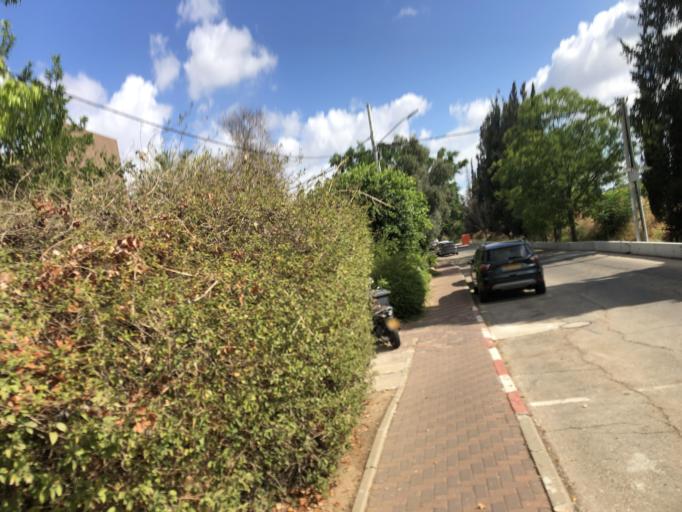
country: IL
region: Central District
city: Yehud
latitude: 32.0340
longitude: 34.8989
